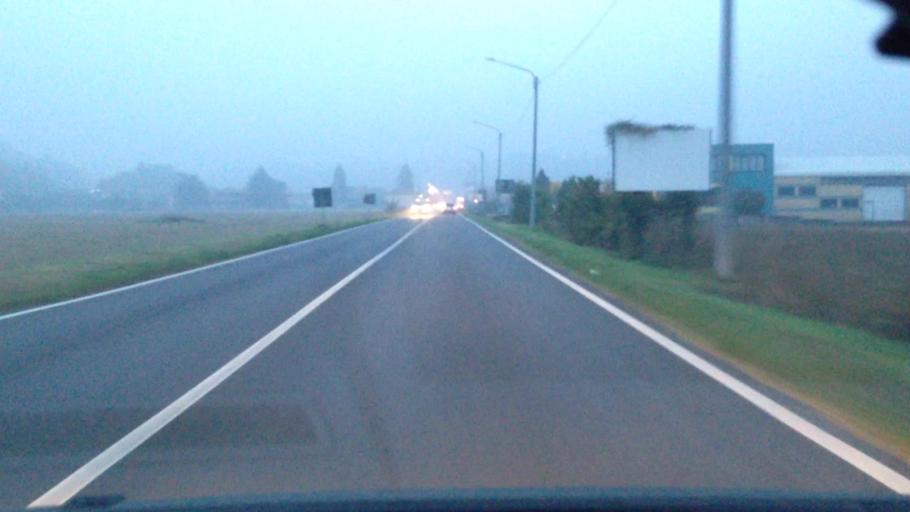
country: IT
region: Piedmont
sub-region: Provincia di Asti
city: Azzano d'Asti
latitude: 44.9071
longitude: 8.2757
